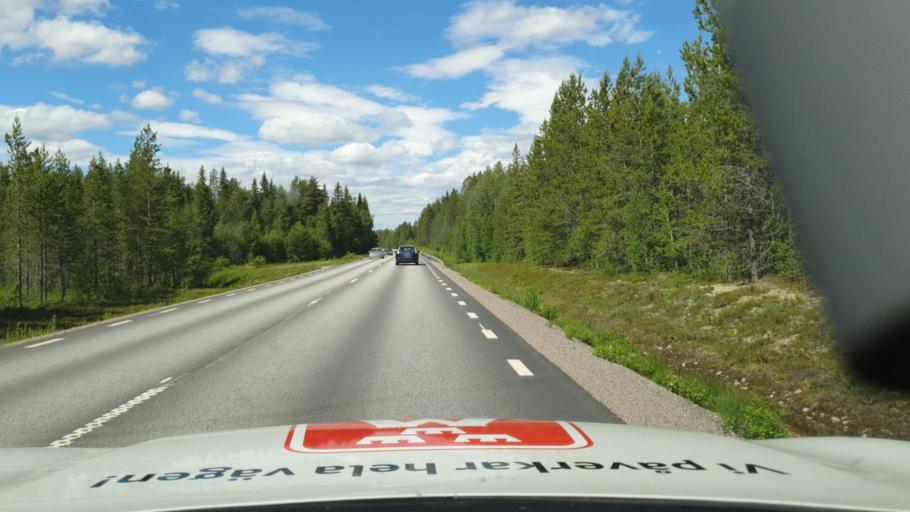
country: SE
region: Vaesterbotten
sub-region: Skelleftea Kommun
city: Langsele
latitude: 65.0290
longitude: 20.1108
